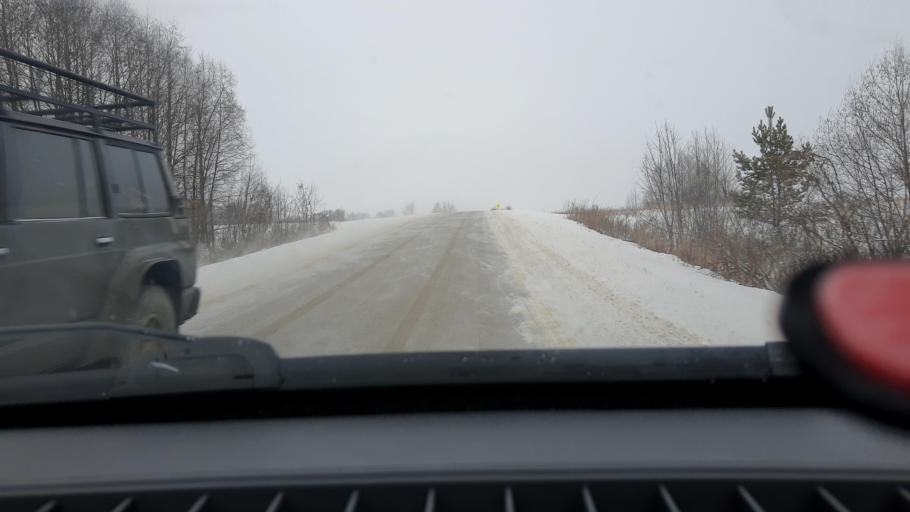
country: RU
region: Bashkortostan
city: Iglino
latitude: 54.7007
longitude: 56.4138
